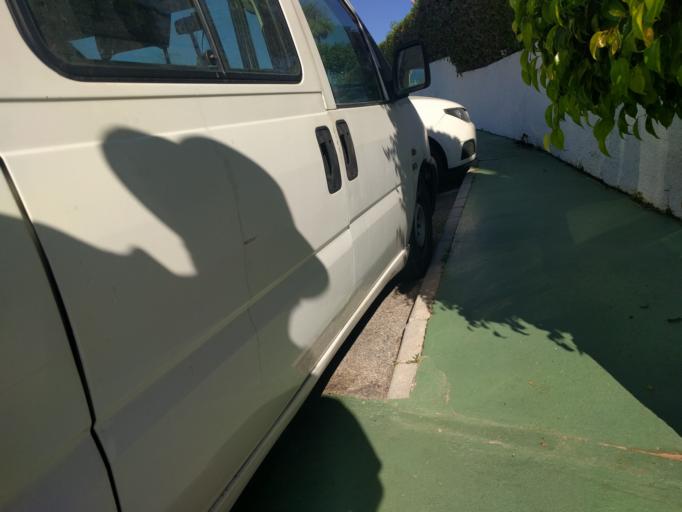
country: ES
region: Andalusia
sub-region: Provincia de Malaga
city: Fuengirola
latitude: 36.5100
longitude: -4.6537
